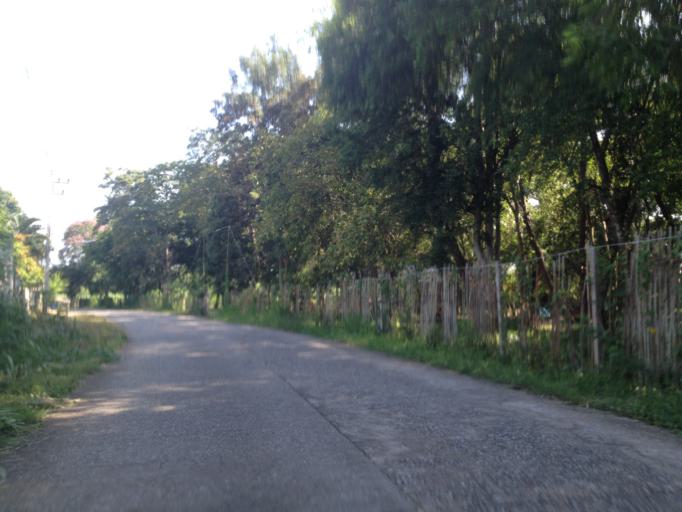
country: TH
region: Chiang Mai
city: Chiang Mai
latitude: 18.7536
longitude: 98.9339
